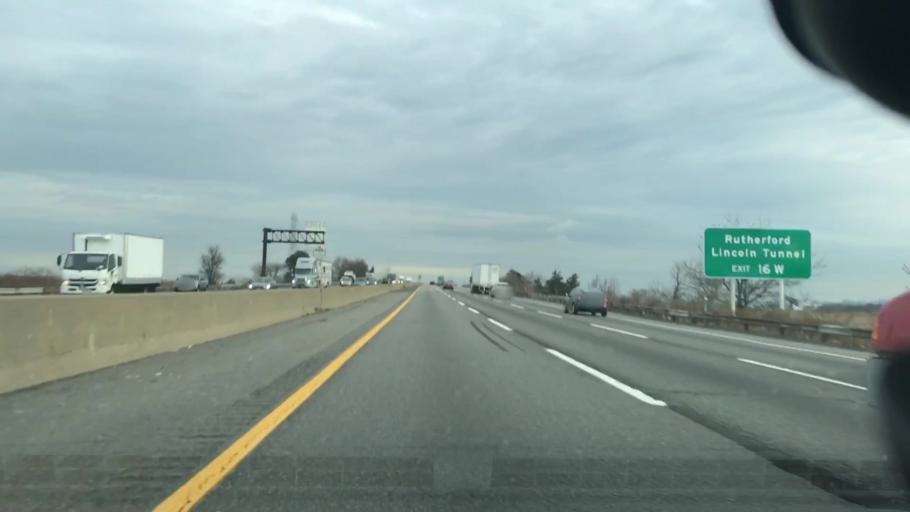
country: US
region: New Jersey
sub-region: Bergen County
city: North Arlington
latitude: 40.7795
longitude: -74.0984
